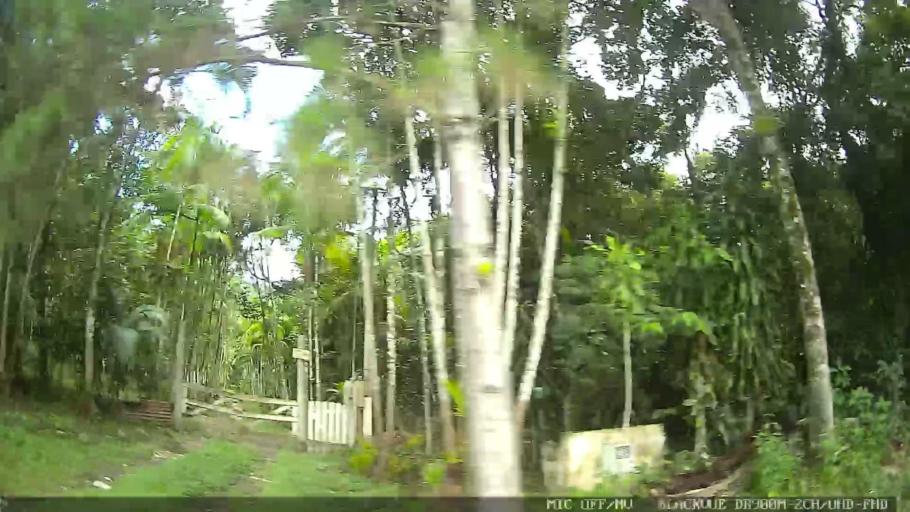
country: BR
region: Sao Paulo
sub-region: Iguape
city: Iguape
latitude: -24.6870
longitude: -47.5116
